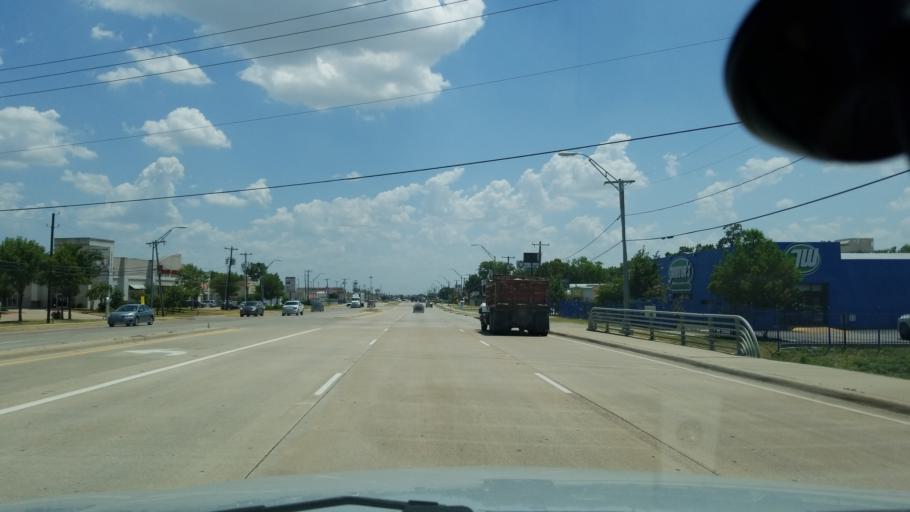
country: US
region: Texas
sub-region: Dallas County
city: Farmers Branch
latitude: 32.9017
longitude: -96.8934
